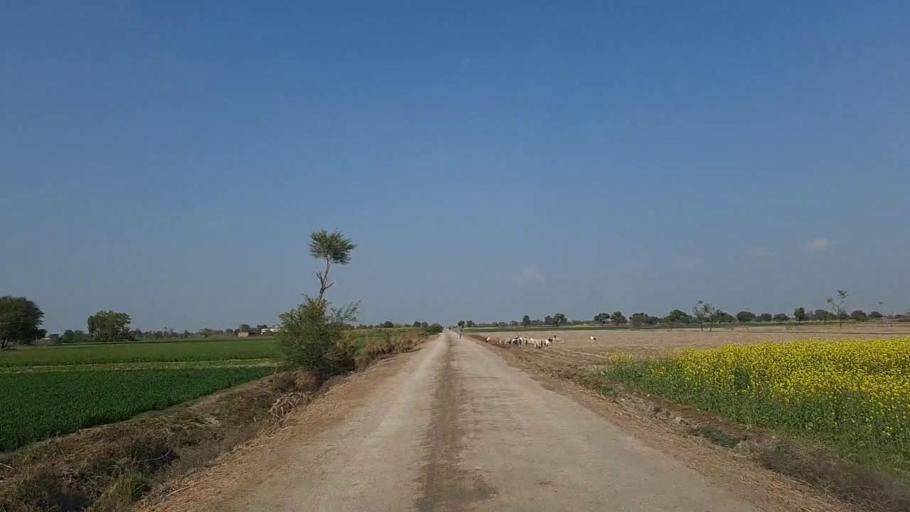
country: PK
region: Sindh
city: Jam Sahib
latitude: 26.2834
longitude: 68.5829
